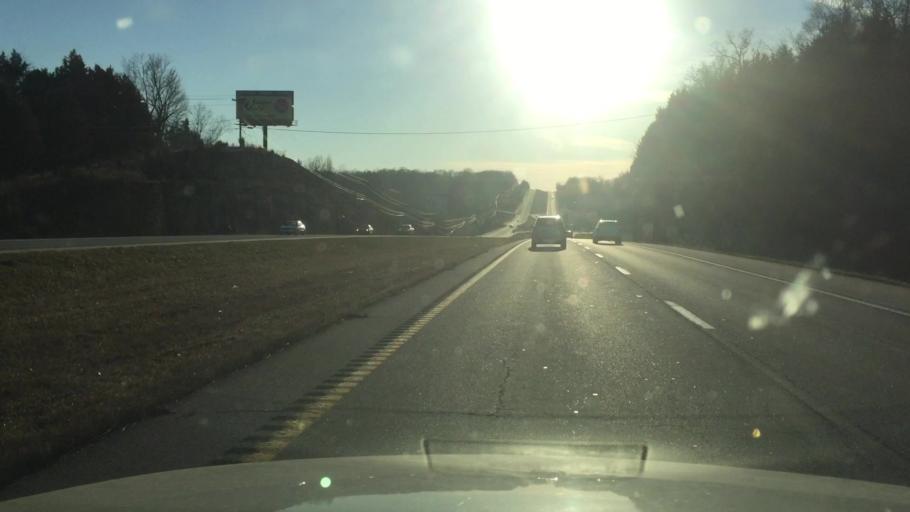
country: US
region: Missouri
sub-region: Cole County
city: Wardsville
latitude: 38.5232
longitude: -92.2283
